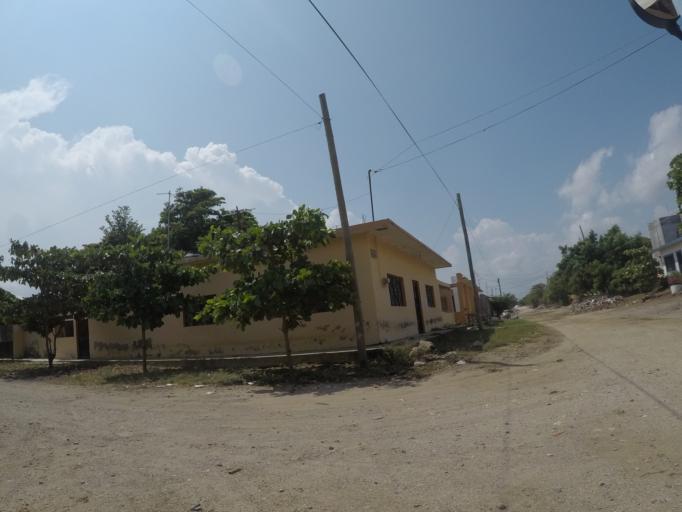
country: MX
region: Oaxaca
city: Union Hidalgo
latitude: 16.4673
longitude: -94.8314
